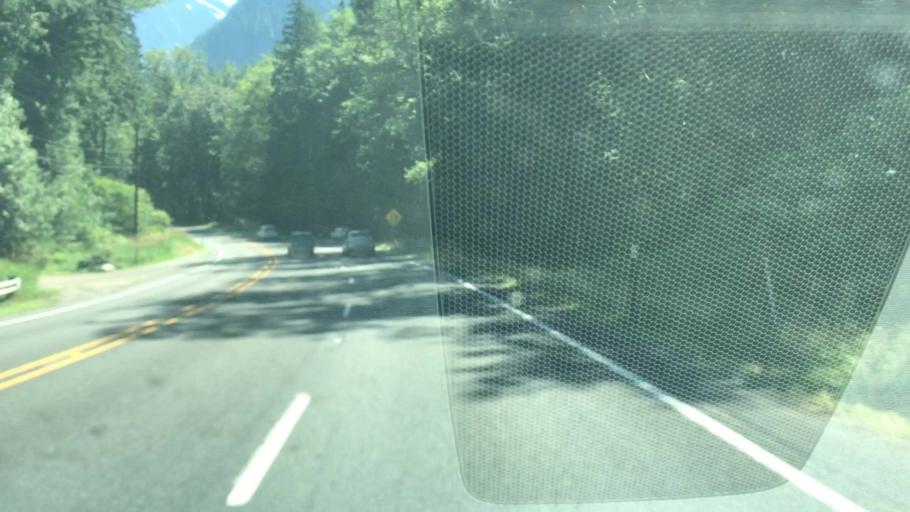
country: US
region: Washington
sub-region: Snohomish County
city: Gold Bar
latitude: 47.8269
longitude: -121.6197
